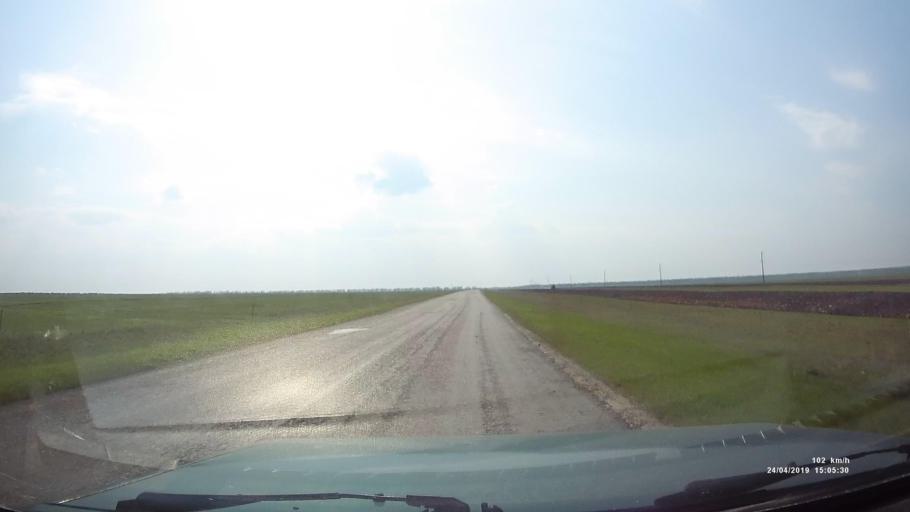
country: RU
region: Rostov
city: Remontnoye
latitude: 46.5600
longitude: 43.4480
